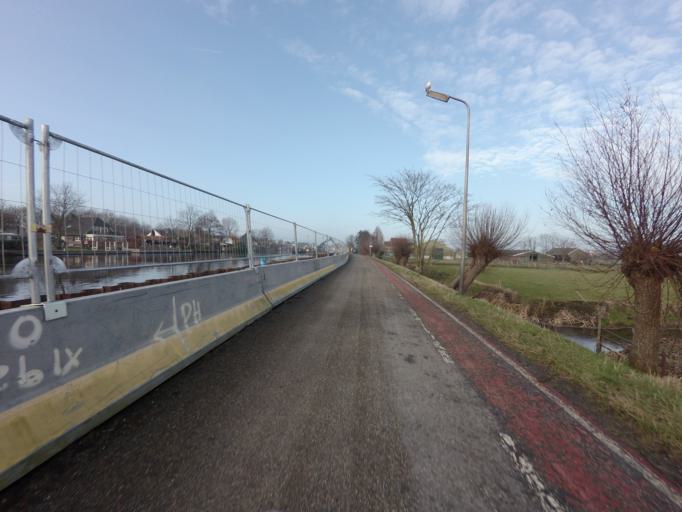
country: NL
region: South Holland
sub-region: Bodegraven-Reeuwijk
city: Bodegraven
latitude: 52.1004
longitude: 4.7367
